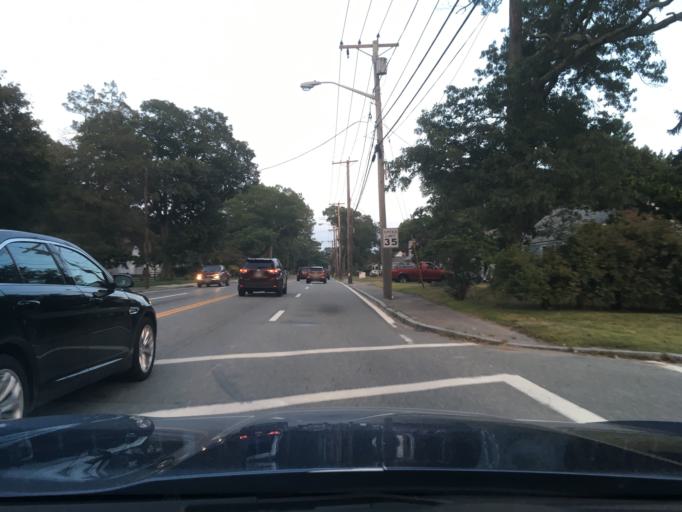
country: US
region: Rhode Island
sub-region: Kent County
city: Warwick
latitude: 41.7066
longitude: -71.4316
